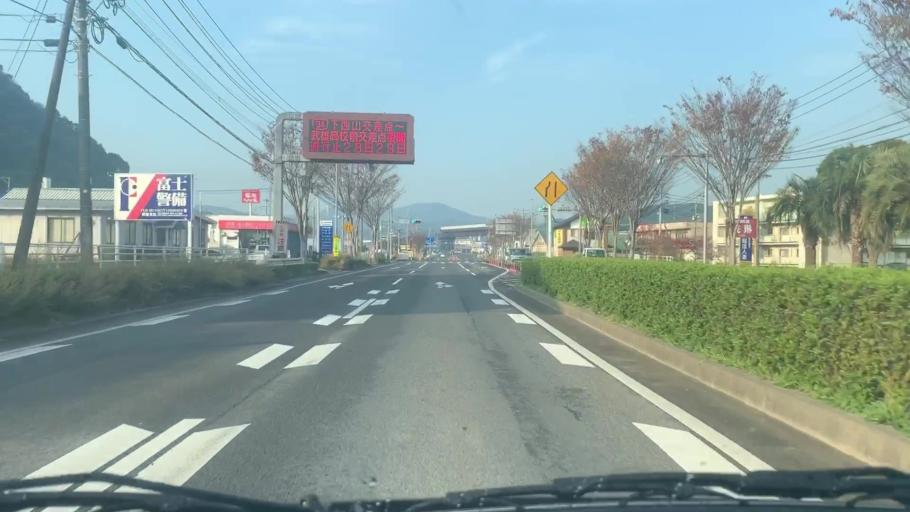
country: JP
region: Saga Prefecture
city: Takeocho-takeo
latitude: 33.1913
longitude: 130.0171
